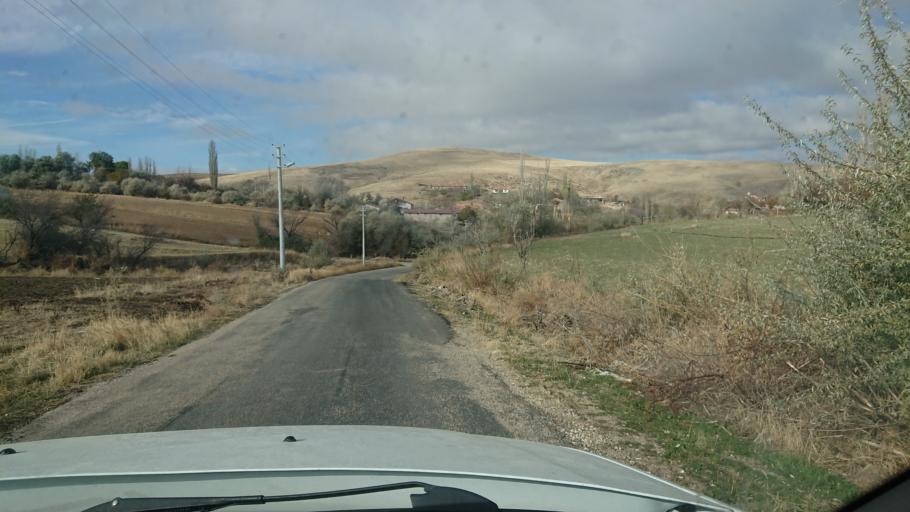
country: TR
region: Aksaray
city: Ortakoy
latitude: 38.8035
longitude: 33.9850
